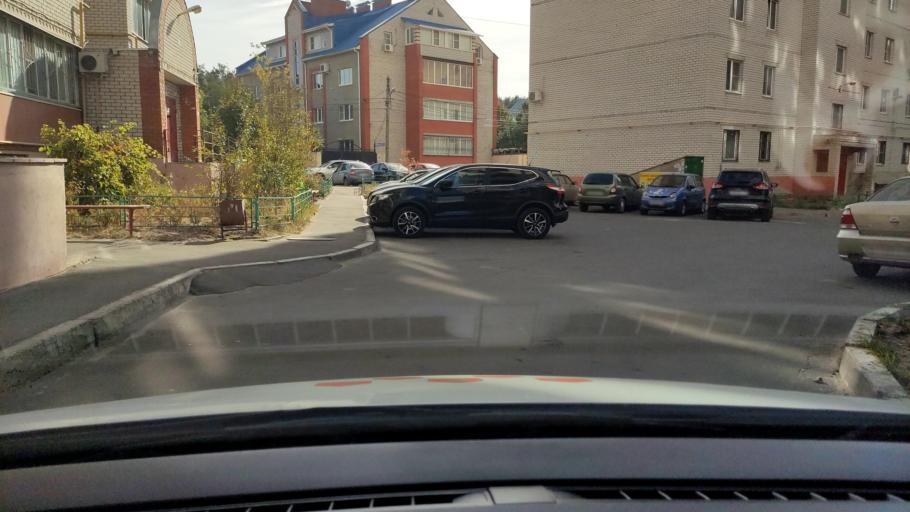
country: RU
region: Voronezj
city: Podgornoye
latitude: 51.7237
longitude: 39.1596
